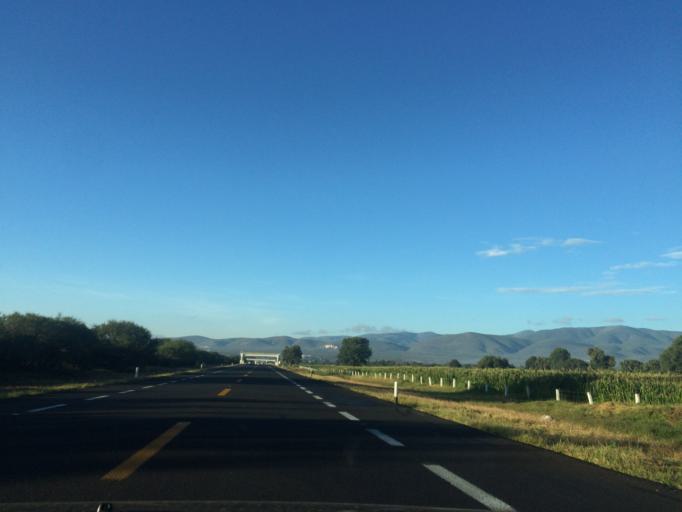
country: MX
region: Puebla
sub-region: Santiago Miahuatlan
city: San Jose Monte Chiquito
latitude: 18.5132
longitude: -97.4544
